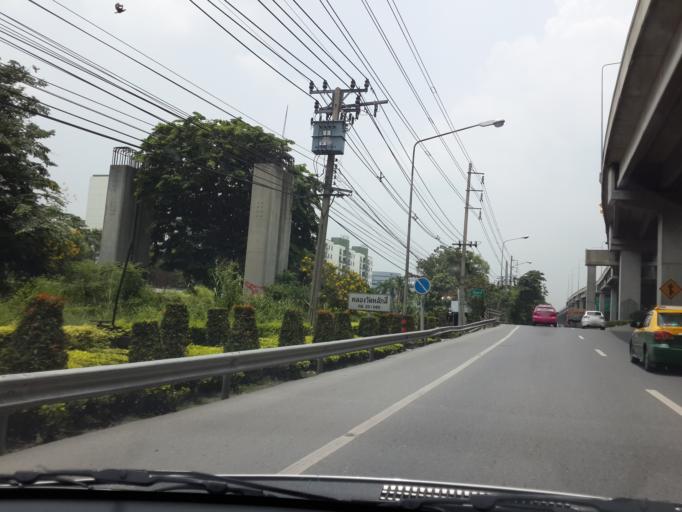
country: TH
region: Bangkok
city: Lak Si
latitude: 13.8900
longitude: 100.5845
